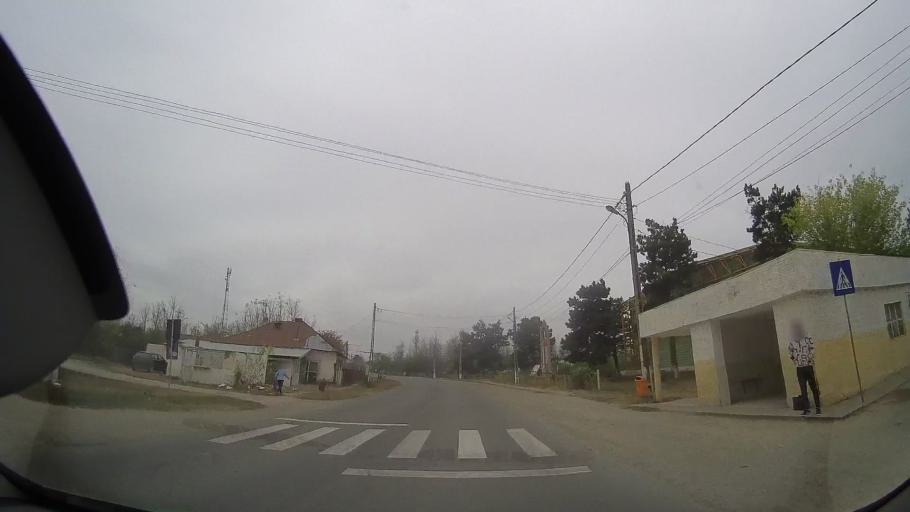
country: RO
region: Ialomita
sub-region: Comuna Grivita
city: Grivita
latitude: 44.7362
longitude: 27.2891
